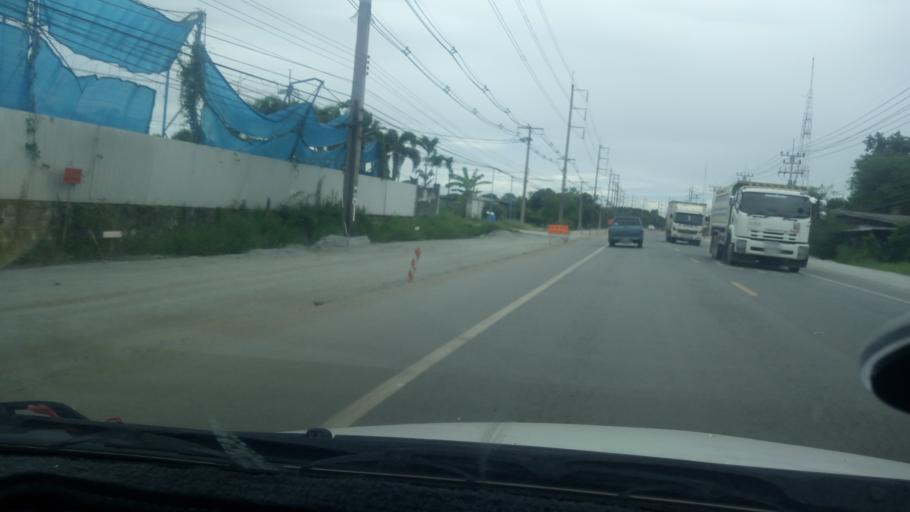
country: TH
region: Chon Buri
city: Phanat Nikhom
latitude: 13.4978
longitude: 101.1630
